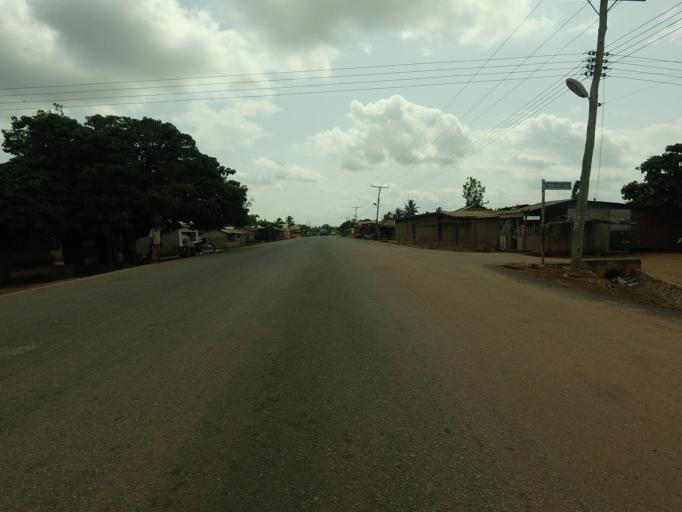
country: TG
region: Maritime
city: Lome
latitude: 6.2225
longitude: 1.0334
